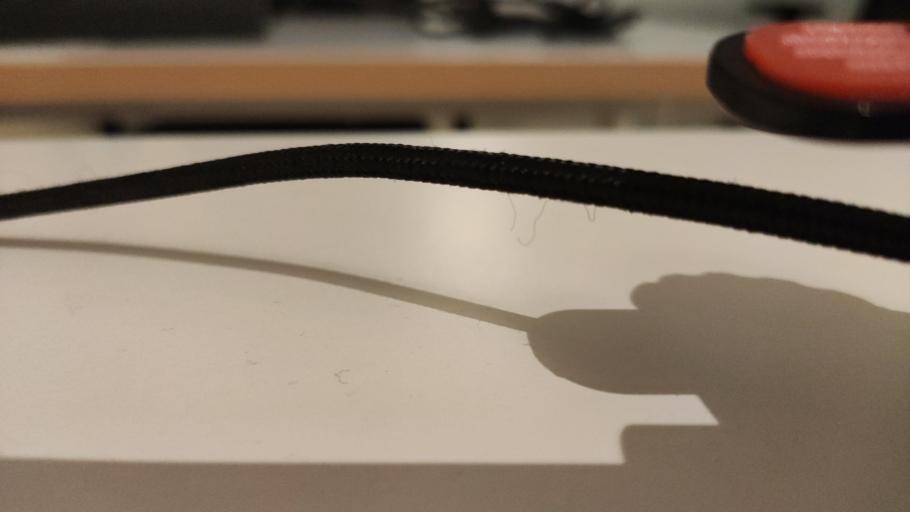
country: RU
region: Moskovskaya
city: Il'inskiy Pogost
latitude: 55.5271
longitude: 38.8722
